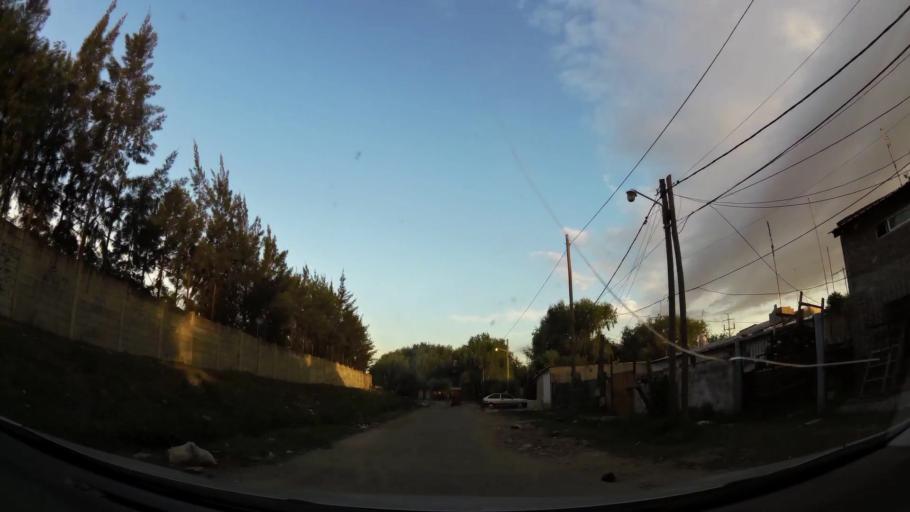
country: AR
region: Buenos Aires
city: Santa Catalina - Dique Lujan
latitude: -34.4387
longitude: -58.6605
